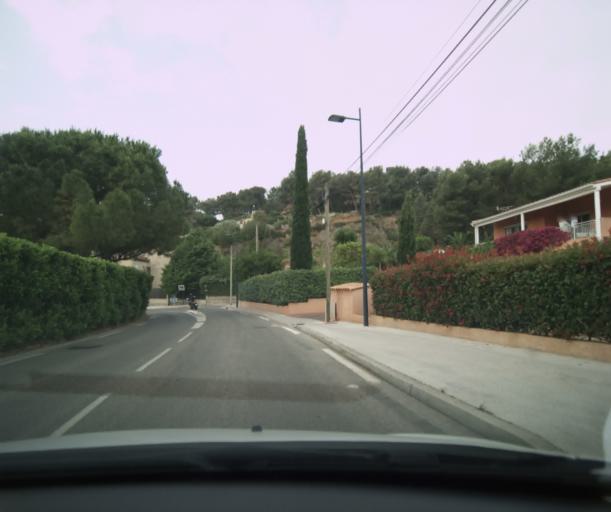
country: FR
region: Provence-Alpes-Cote d'Azur
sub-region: Departement du Var
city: Carqueiranne
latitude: 43.1002
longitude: 6.0799
